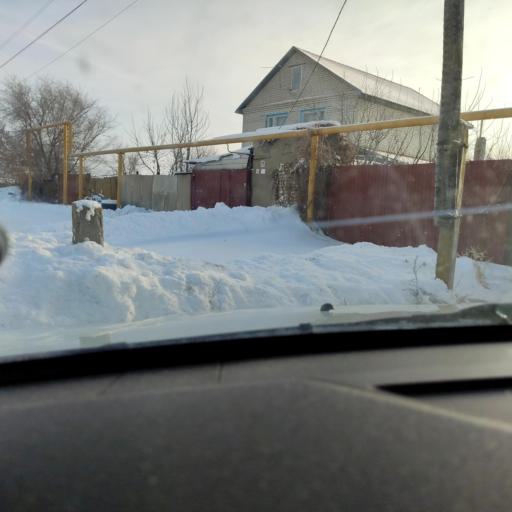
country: RU
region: Samara
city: Smyshlyayevka
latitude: 53.1650
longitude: 50.3892
